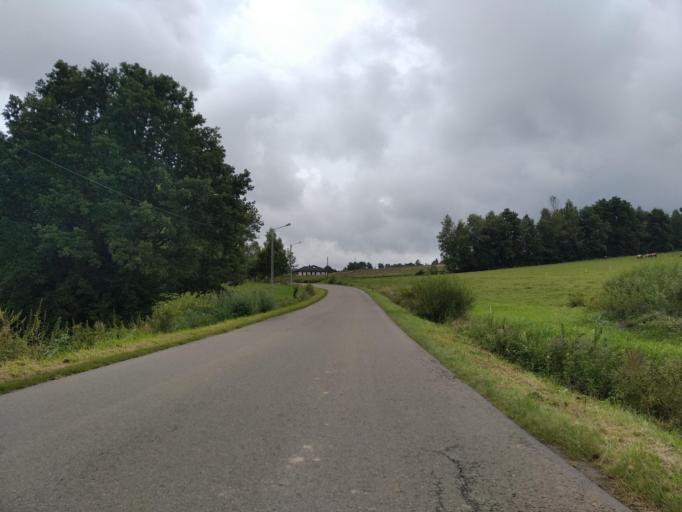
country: PL
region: Subcarpathian Voivodeship
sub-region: Powiat brzozowski
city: Nozdrzec
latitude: 49.7302
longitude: 22.2728
